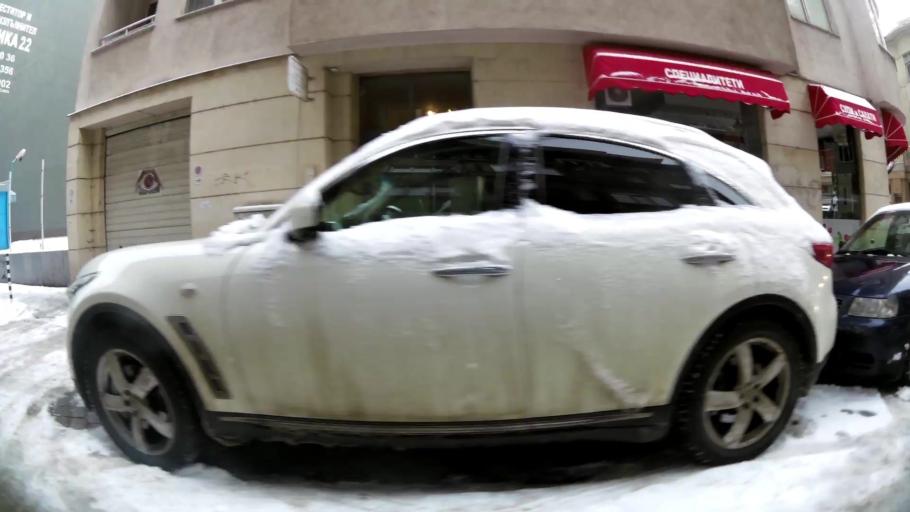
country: BG
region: Sofia-Capital
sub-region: Stolichna Obshtina
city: Sofia
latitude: 42.7003
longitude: 23.3254
